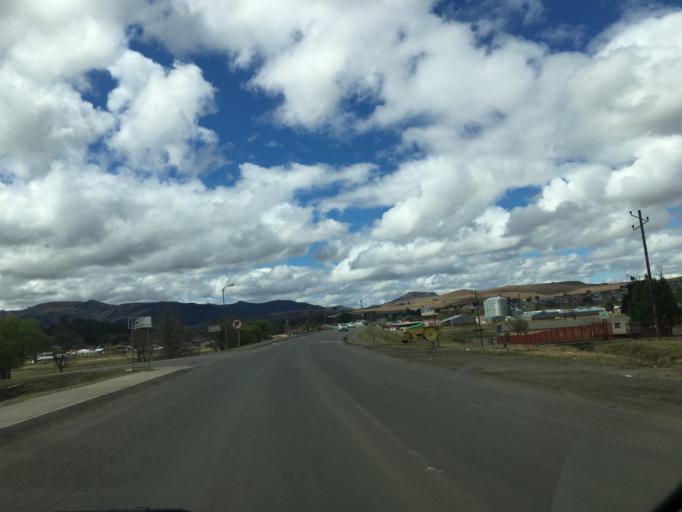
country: ZA
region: Eastern Cape
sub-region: Chris Hani District Municipality
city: Elliot
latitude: -31.3370
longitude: 27.8403
